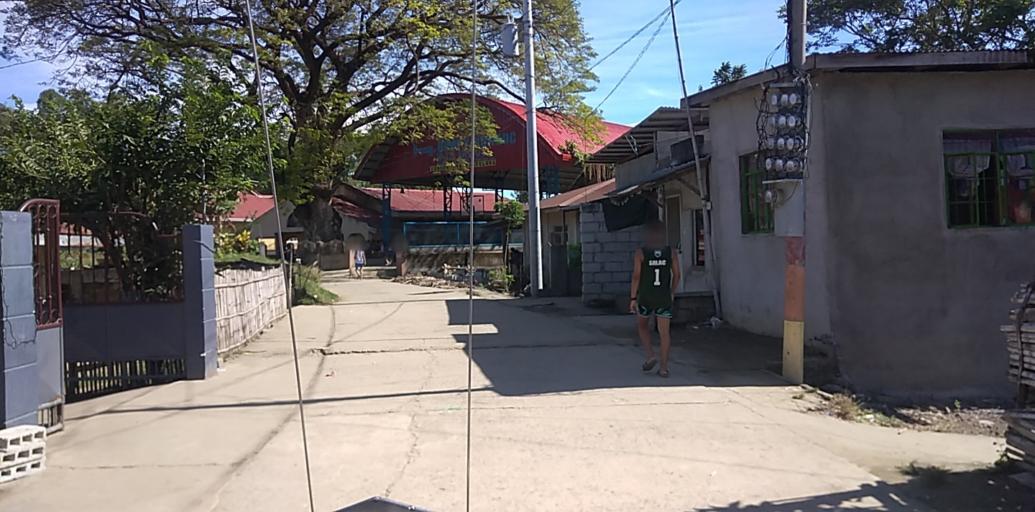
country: PH
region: Central Luzon
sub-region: Province of Pampanga
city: San Nicolas
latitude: 15.0641
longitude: 120.8136
